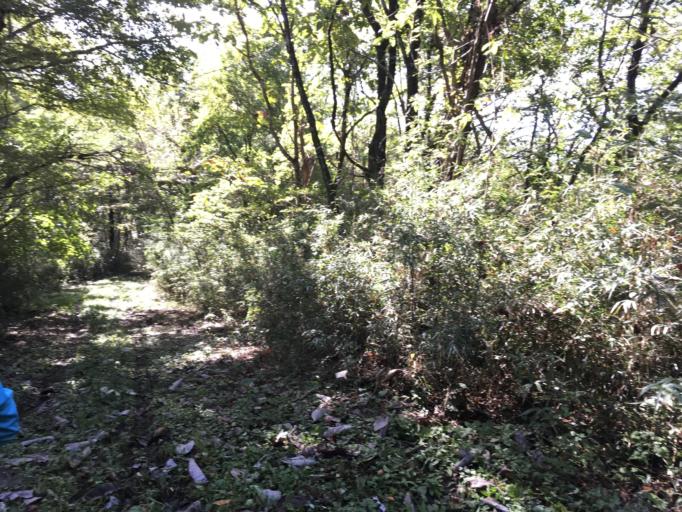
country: JP
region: Iwate
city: Ichinoseki
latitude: 38.8832
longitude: 141.1256
